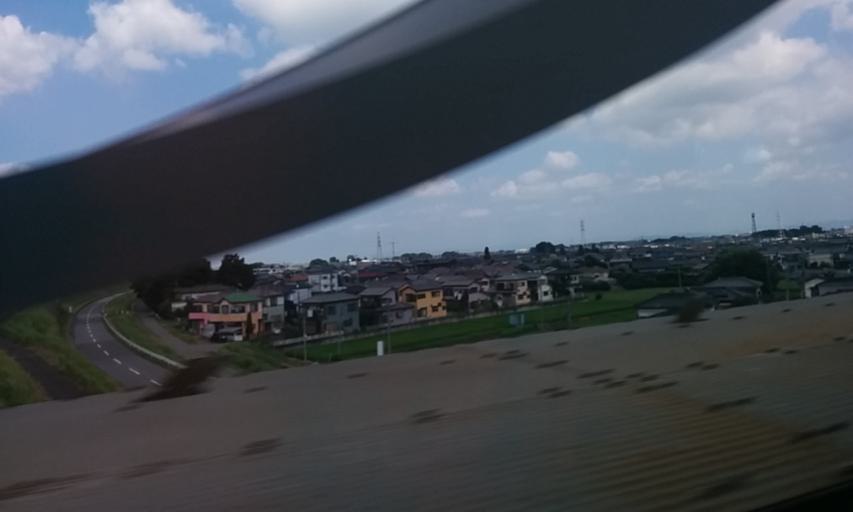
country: JP
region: Saitama
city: Kurihashi
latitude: 36.1378
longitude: 139.7209
